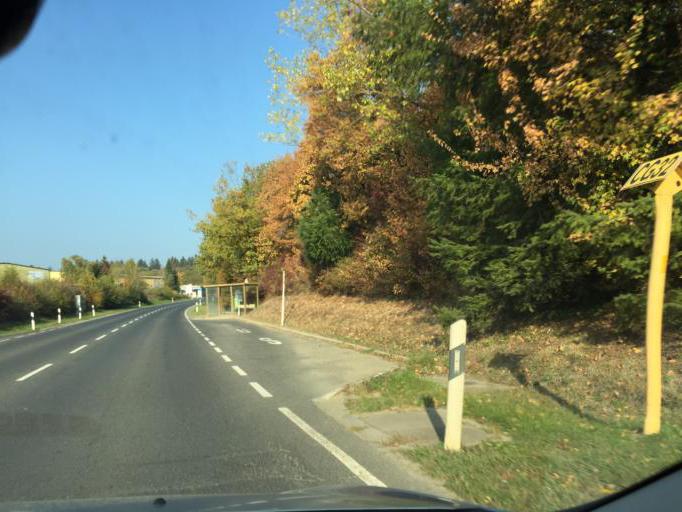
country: LU
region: Luxembourg
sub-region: Canton de Luxembourg
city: Sandweiler
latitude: 49.6066
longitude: 6.2044
